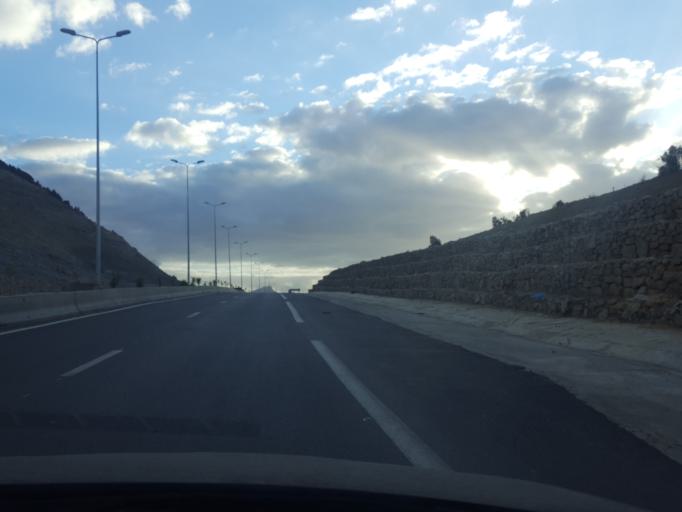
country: TN
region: Tunis
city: Hammam-Lif
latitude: 36.6943
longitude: 10.3976
